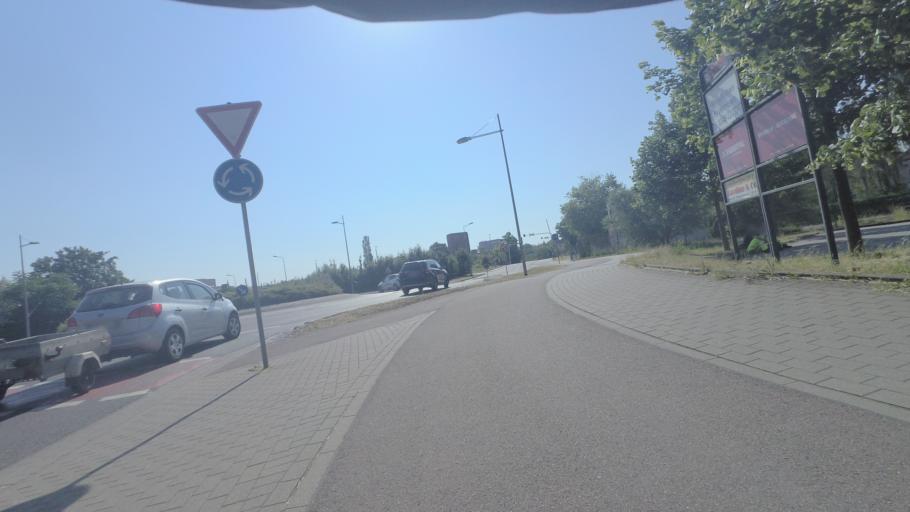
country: DE
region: Saxony-Anhalt
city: Dessau
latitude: 51.8354
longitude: 12.2288
